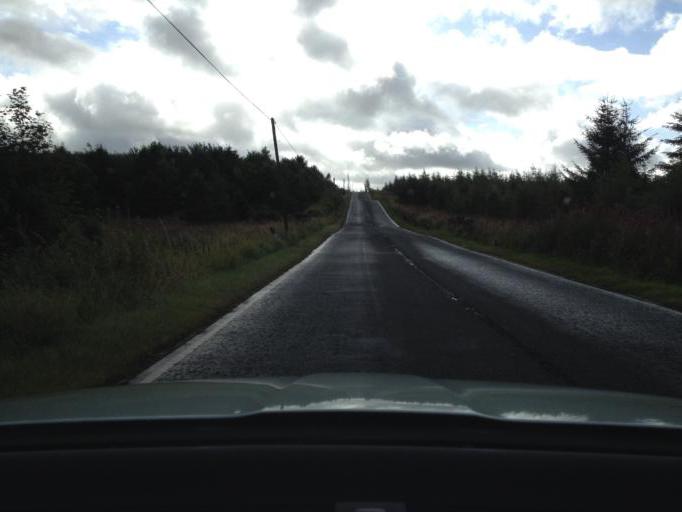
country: GB
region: Scotland
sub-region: West Lothian
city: West Calder
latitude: 55.8215
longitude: -3.5263
